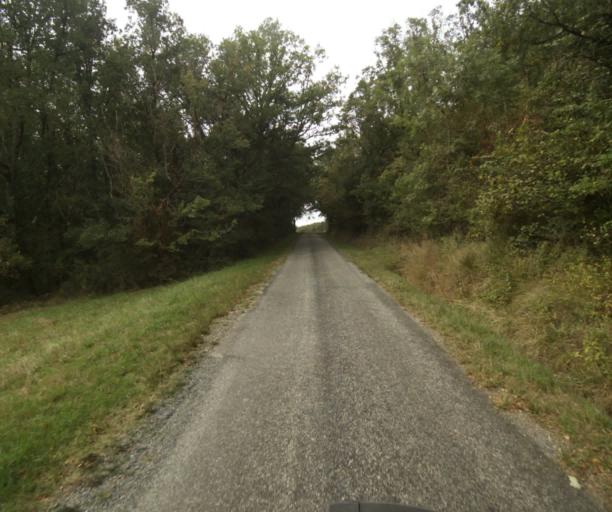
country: FR
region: Midi-Pyrenees
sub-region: Departement du Tarn-et-Garonne
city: Beaumont-de-Lomagne
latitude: 43.8284
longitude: 1.0773
